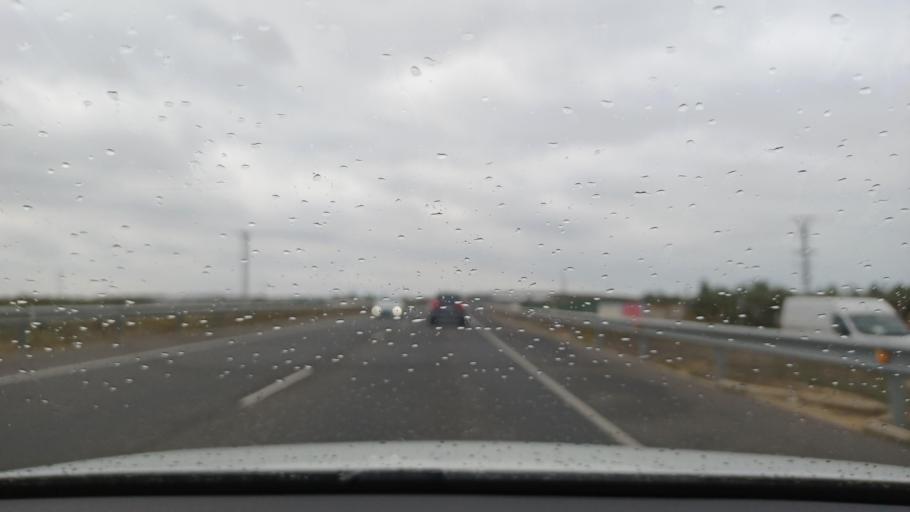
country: ES
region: Valencia
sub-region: Provincia de Castello
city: Benicarlo
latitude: 40.4192
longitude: 0.3877
